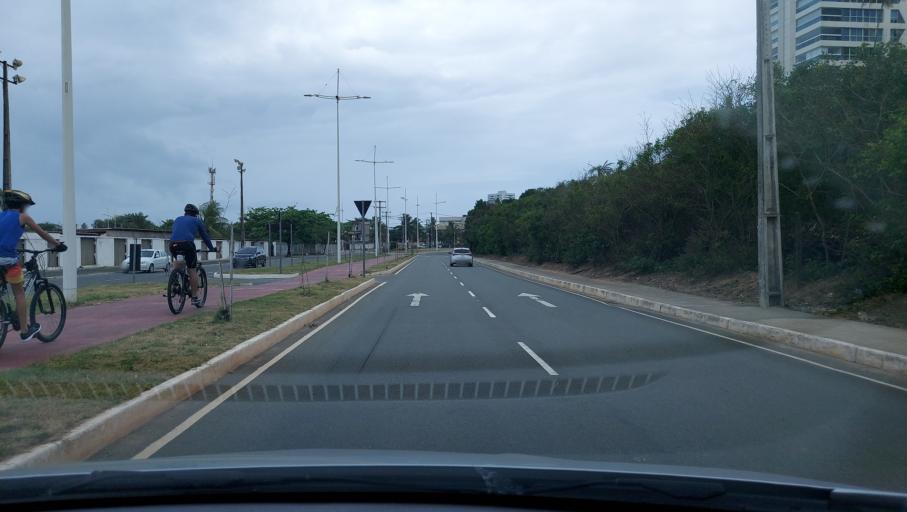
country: BR
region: Bahia
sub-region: Lauro De Freitas
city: Lauro de Freitas
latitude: -12.9609
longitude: -38.4026
